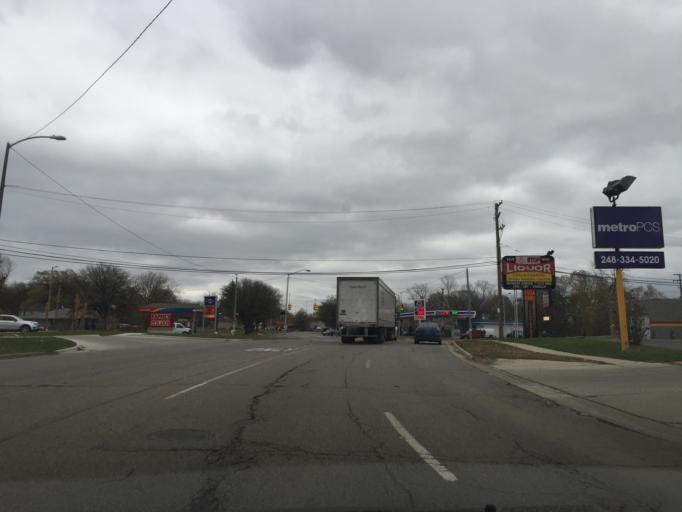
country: US
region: Michigan
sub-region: Oakland County
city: Pontiac
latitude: 42.6573
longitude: -83.3011
